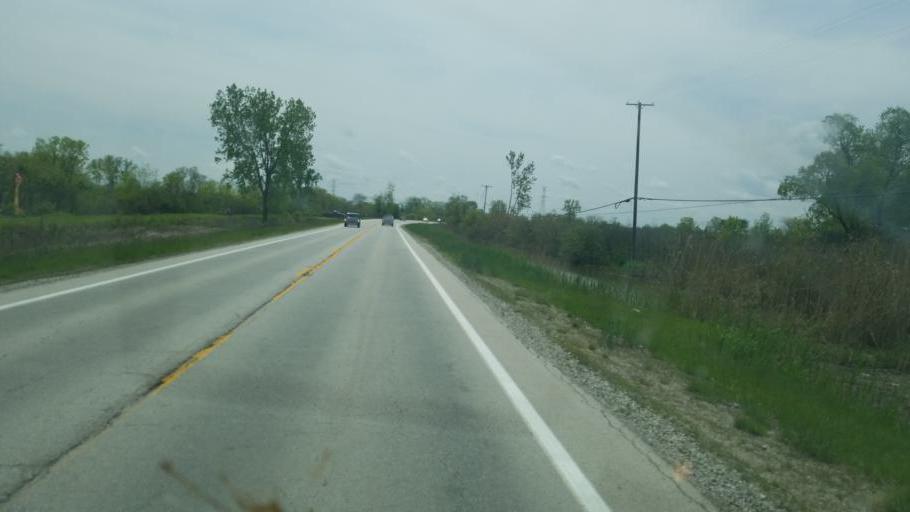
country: US
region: Ohio
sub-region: Ottawa County
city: Oak Harbor
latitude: 41.4505
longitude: -83.0555
